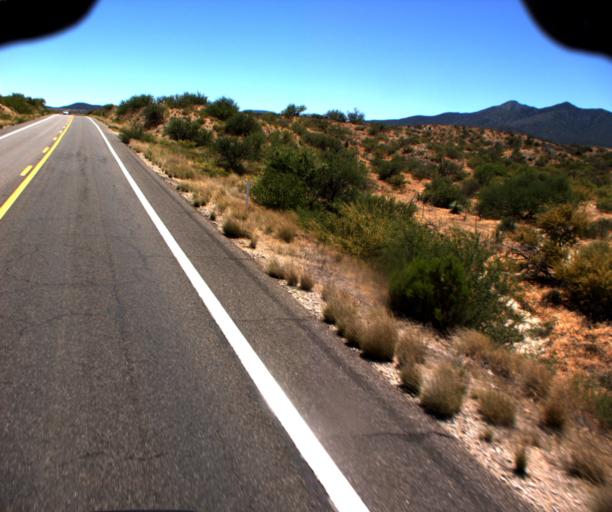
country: US
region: Arizona
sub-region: Gila County
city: Globe
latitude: 33.3594
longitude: -110.7358
